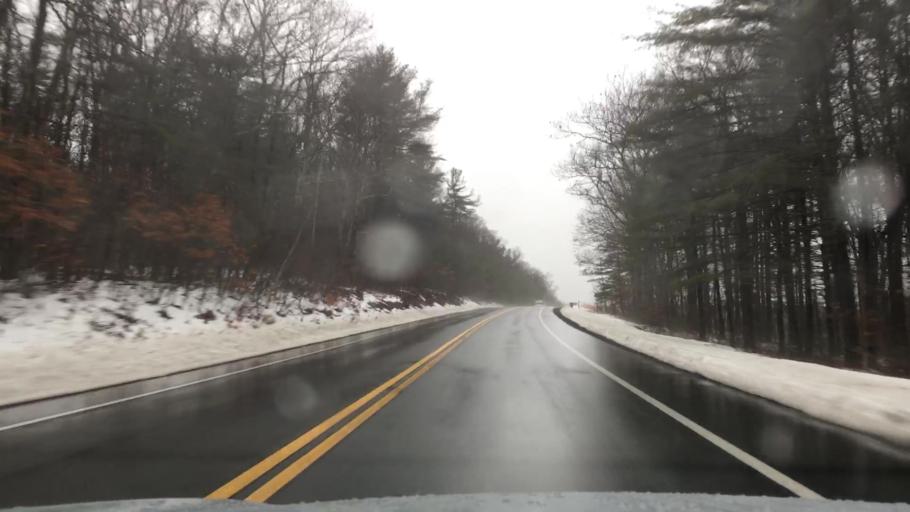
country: US
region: Massachusetts
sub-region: Hampshire County
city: Pelham
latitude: 42.3991
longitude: -72.4044
